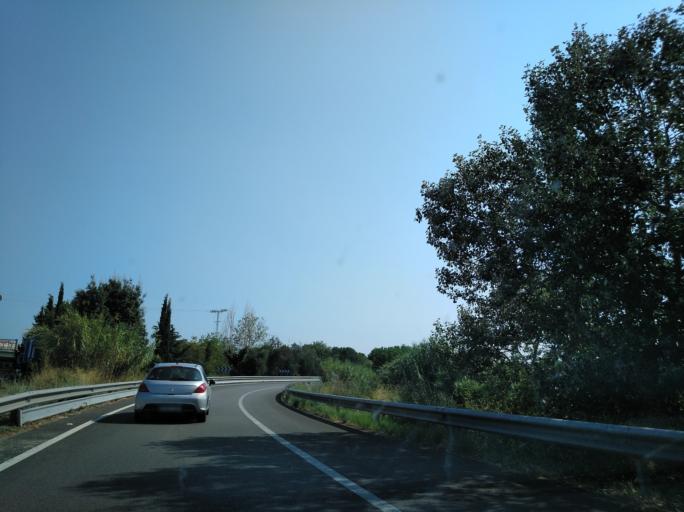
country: ES
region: Catalonia
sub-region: Provincia de Barcelona
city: Argentona
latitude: 41.5472
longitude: 2.4134
